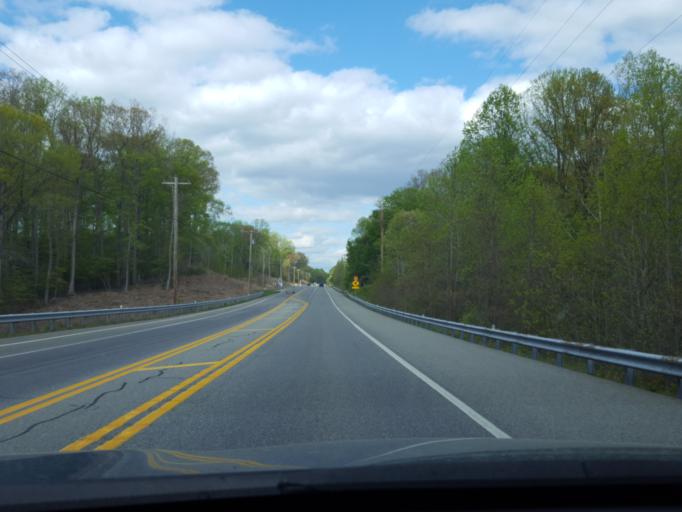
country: US
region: Maryland
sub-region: Charles County
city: Saint Charles
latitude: 38.5523
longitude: -76.8932
